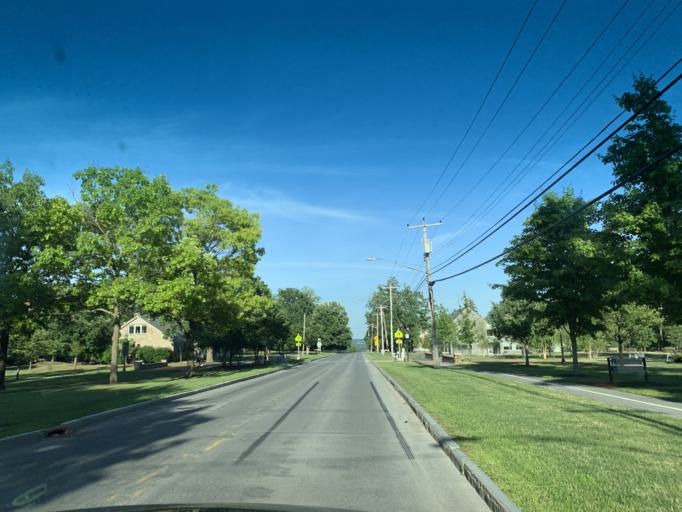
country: US
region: New York
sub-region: Oneida County
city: Clinton
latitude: 43.0506
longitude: -75.4084
